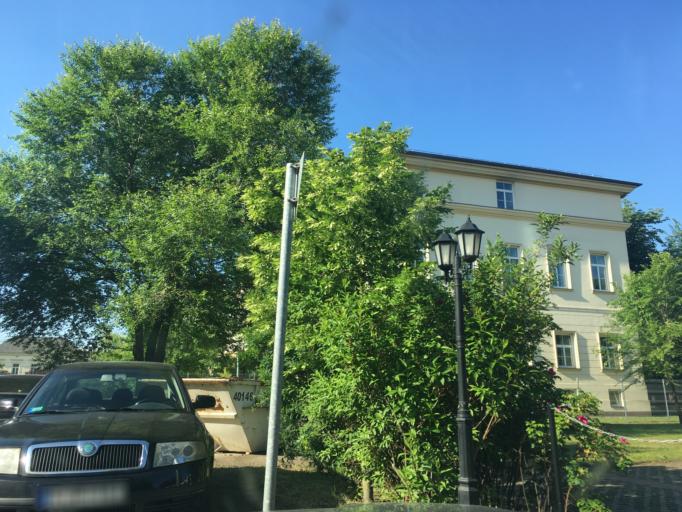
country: HU
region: Hajdu-Bihar
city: Debrecen
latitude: 47.5283
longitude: 21.6432
